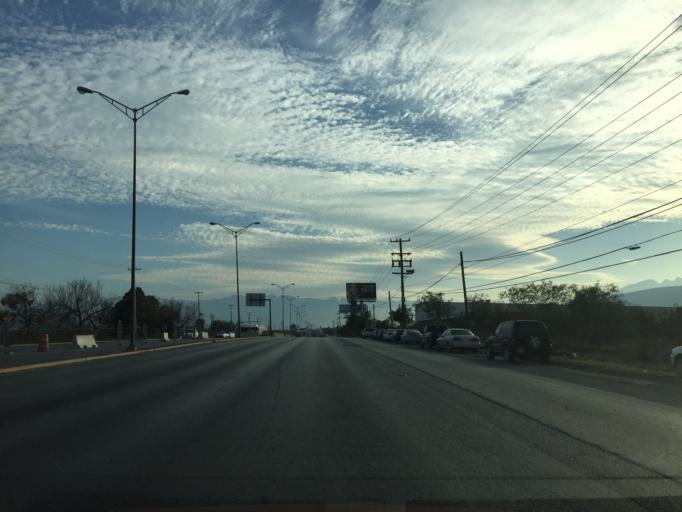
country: MX
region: Nuevo Leon
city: General Escobedo
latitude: 25.7948
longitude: -100.2799
